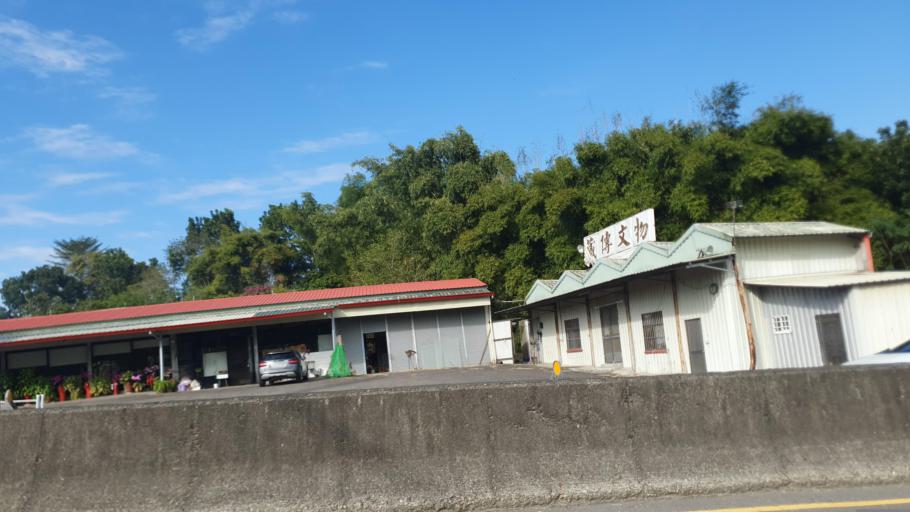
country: TW
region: Taiwan
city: Yujing
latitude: 23.0532
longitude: 120.4056
